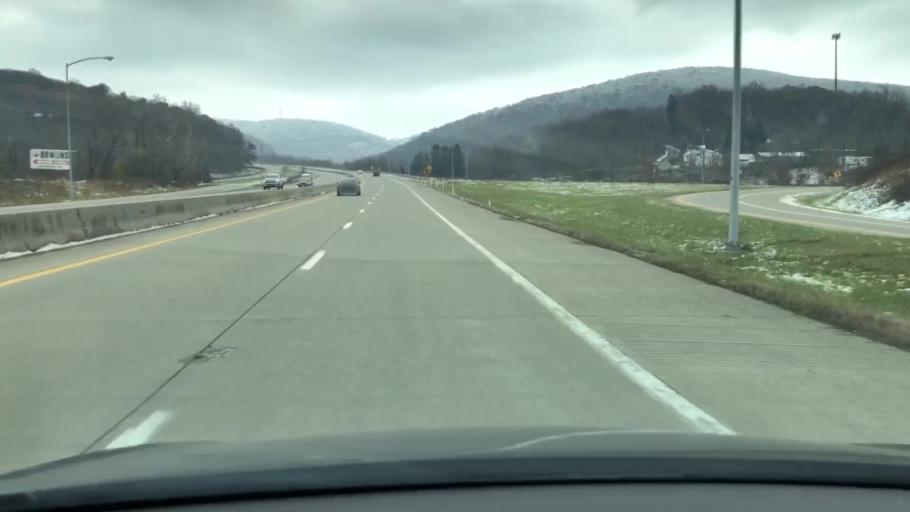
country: US
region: Pennsylvania
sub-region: Fayette County
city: Hopwood
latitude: 39.8708
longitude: -79.7006
